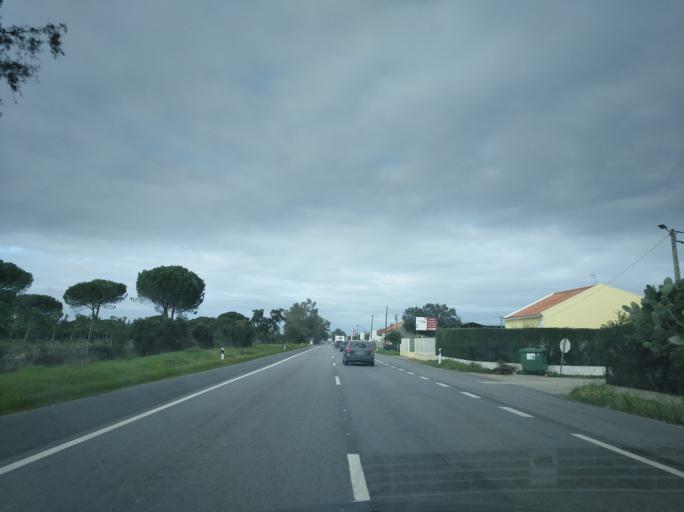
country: PT
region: Setubal
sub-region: Grandola
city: Grandola
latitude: 38.1960
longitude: -8.5650
